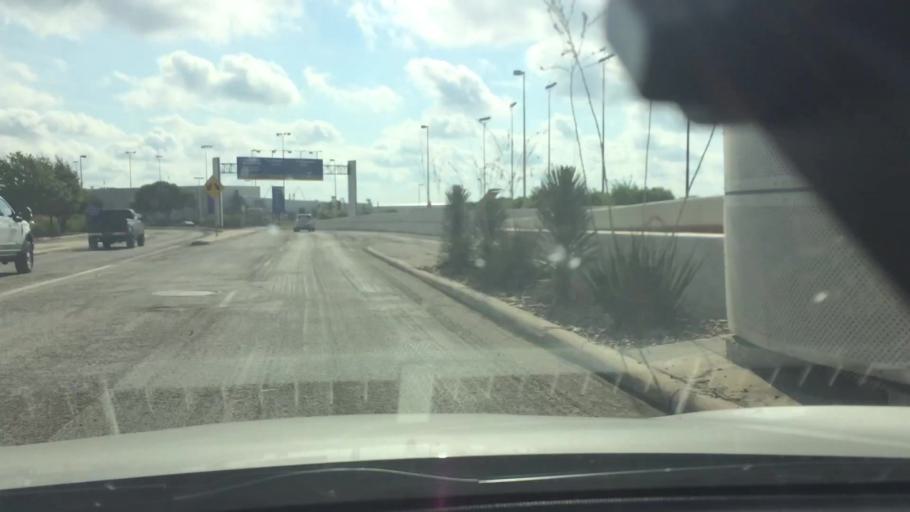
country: US
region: Texas
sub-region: Bexar County
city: Alamo Heights
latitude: 29.5254
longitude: -98.4743
